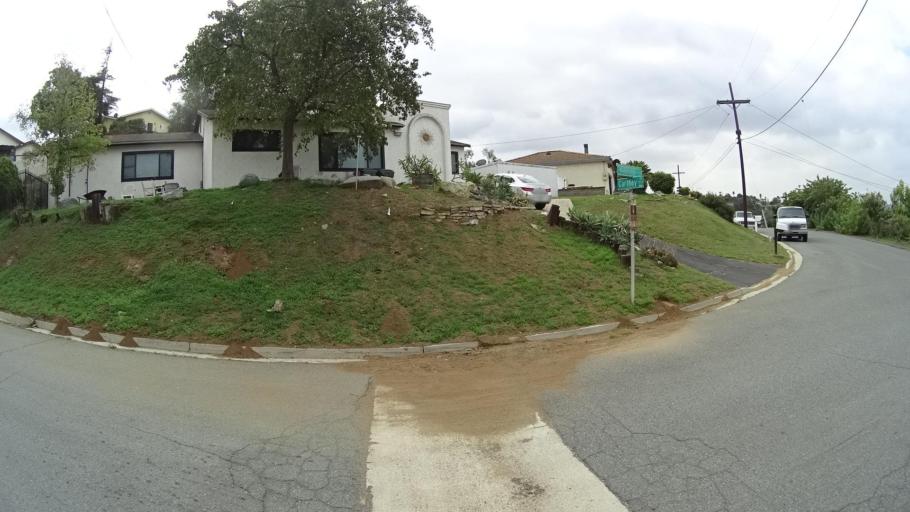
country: US
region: California
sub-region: San Diego County
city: Spring Valley
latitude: 32.7526
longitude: -116.9974
